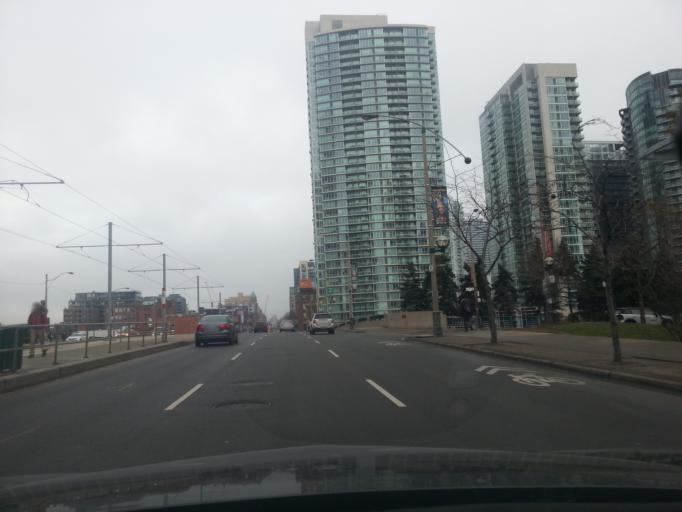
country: CA
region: Ontario
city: Toronto
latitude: 43.6409
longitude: -79.3930
